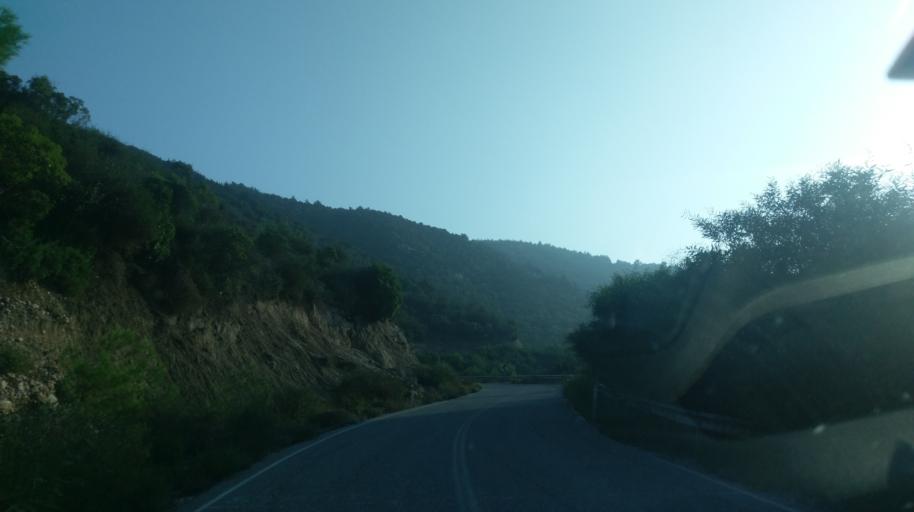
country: CY
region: Ammochostos
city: Trikomo
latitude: 35.4035
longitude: 33.9042
